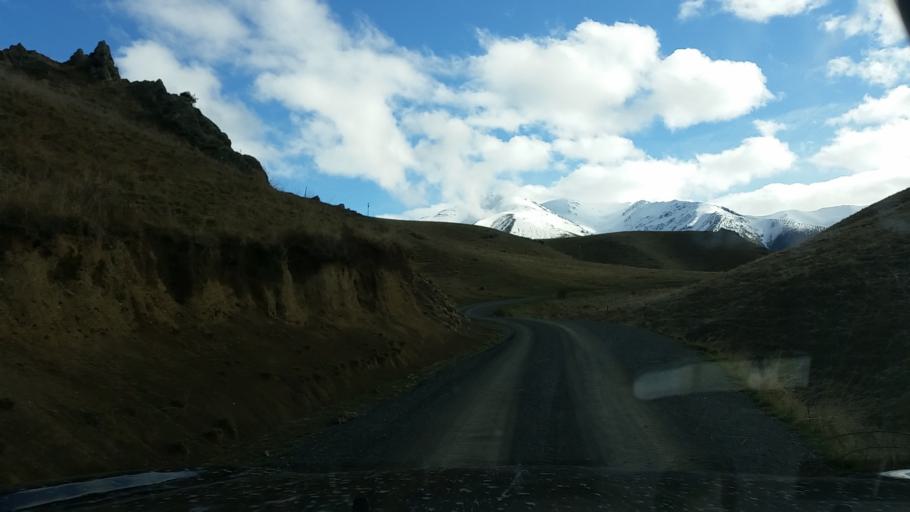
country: NZ
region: Canterbury
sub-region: Kaikoura District
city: Kaikoura
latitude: -42.0410
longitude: 173.3764
